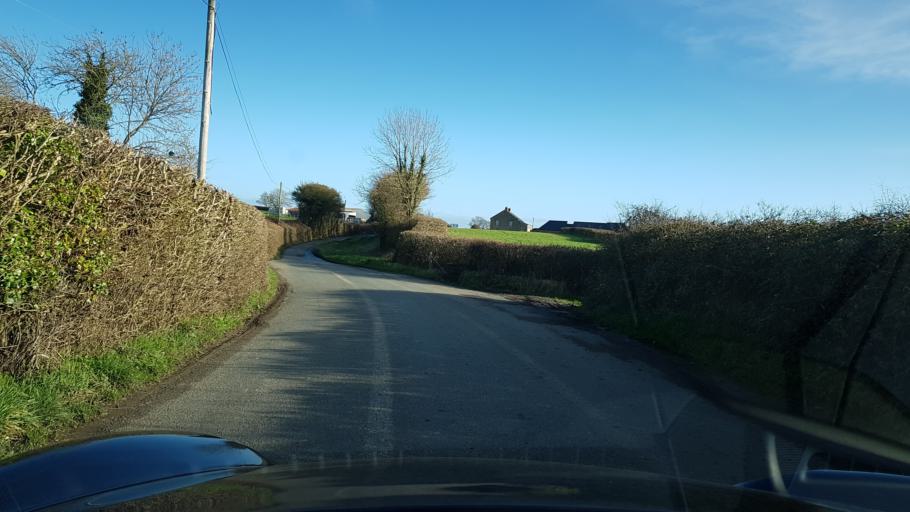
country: GB
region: England
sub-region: Dorset
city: Bridport
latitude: 50.7792
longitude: -2.8277
